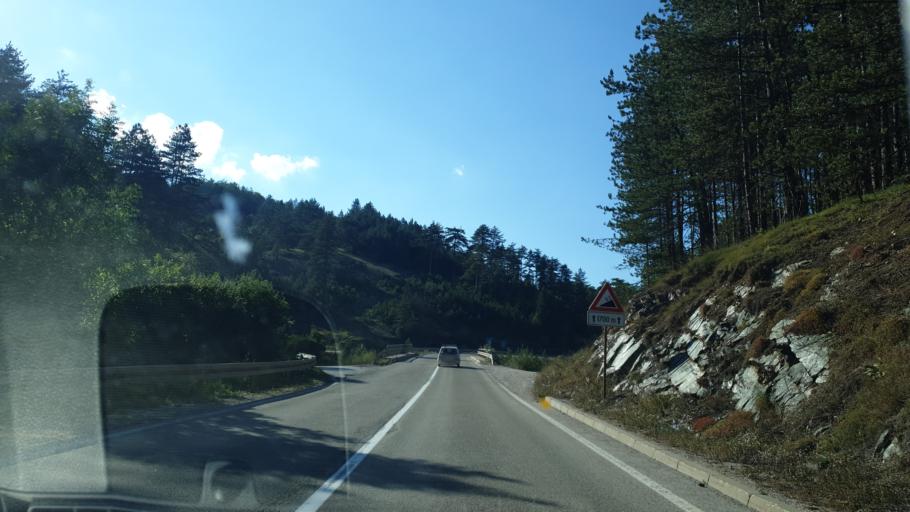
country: RS
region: Central Serbia
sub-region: Zlatiborski Okrug
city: Nova Varos
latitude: 43.5518
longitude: 19.7765
